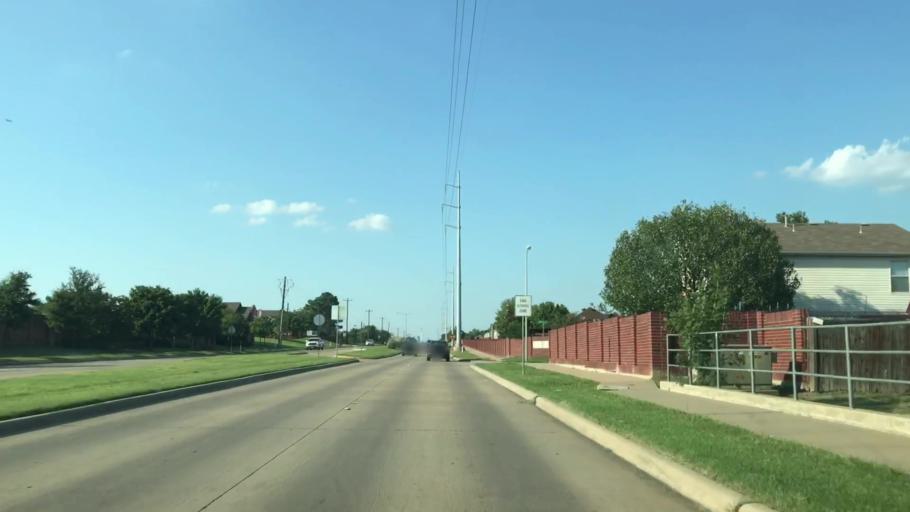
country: US
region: Texas
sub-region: Denton County
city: Lewisville
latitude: 33.0330
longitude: -97.0360
